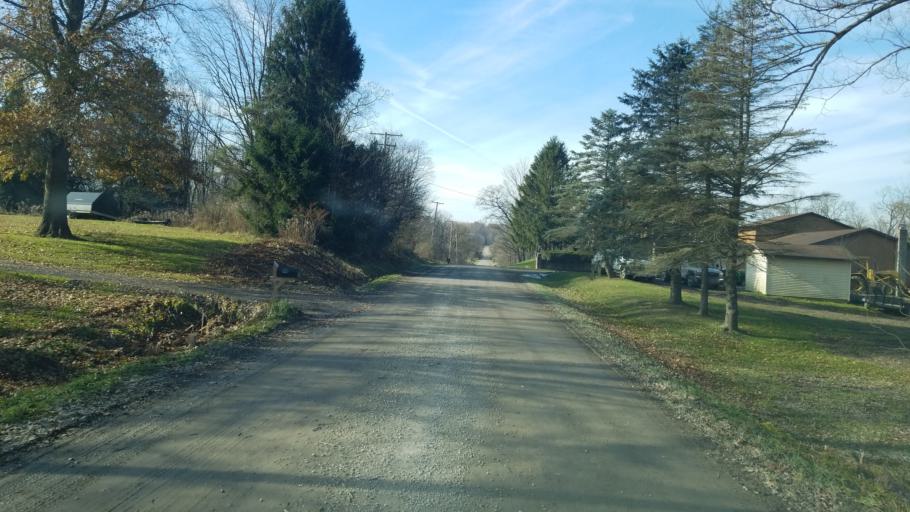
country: US
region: Ohio
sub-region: Ashtabula County
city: Roaming Shores
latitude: 41.6780
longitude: -80.8989
